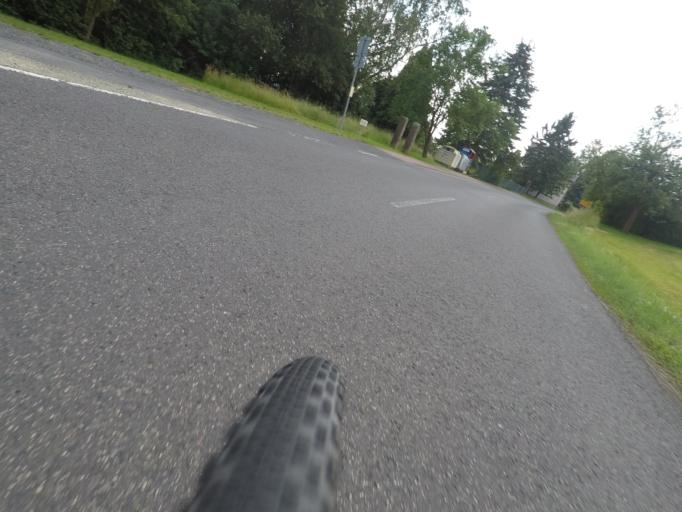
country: DE
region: Hesse
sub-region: Regierungsbezirk Kassel
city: Bad Sooden-Allendorf
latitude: 51.2427
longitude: 9.8952
